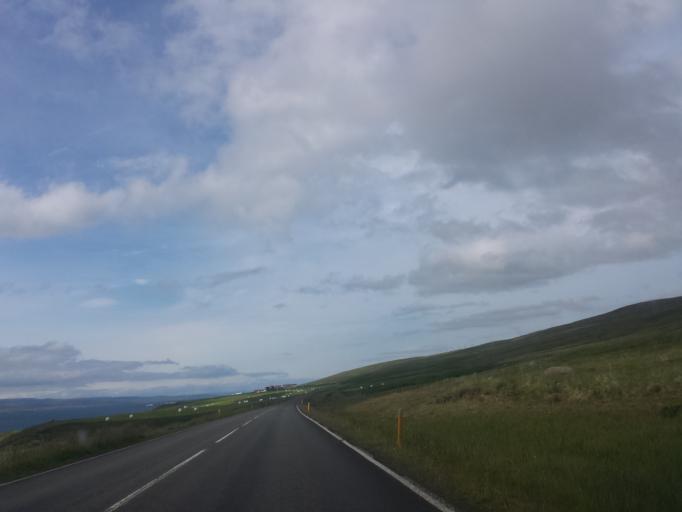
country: IS
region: West
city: Borgarnes
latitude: 65.2157
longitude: -21.0696
